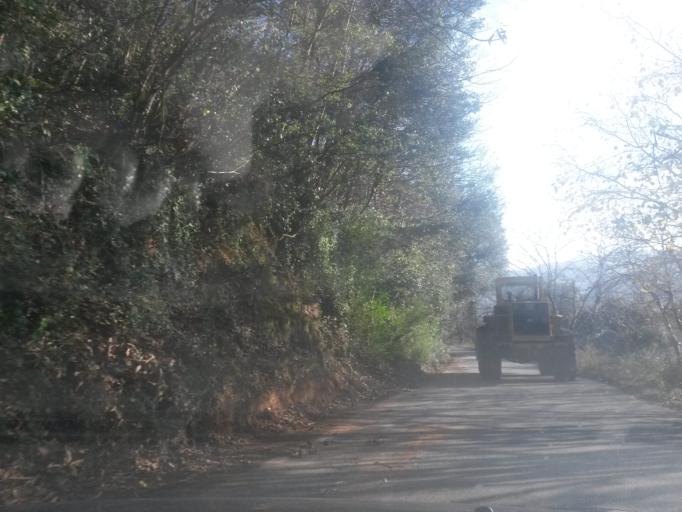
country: ES
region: Catalonia
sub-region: Provincia de Girona
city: Susqueda
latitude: 41.9579
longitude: 2.5454
